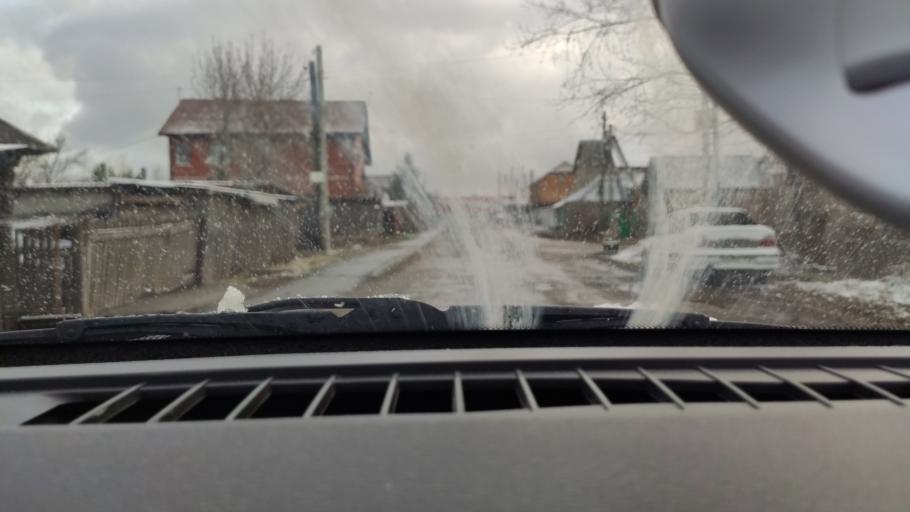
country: RU
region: Perm
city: Kondratovo
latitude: 57.9825
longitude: 56.1007
